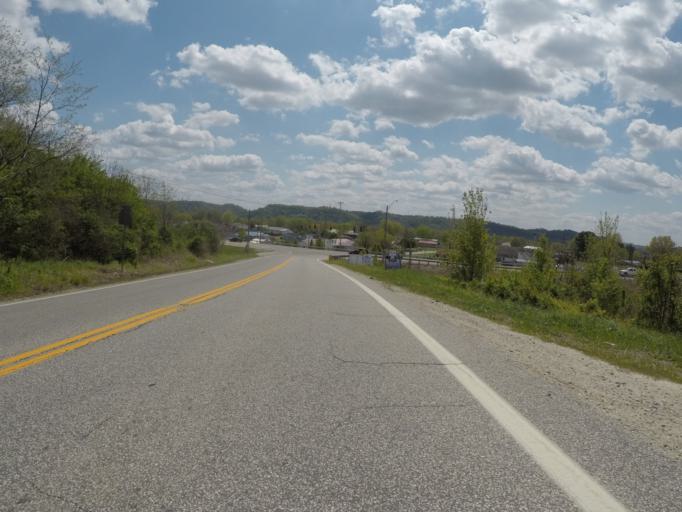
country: US
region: West Virginia
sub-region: Cabell County
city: Pea Ridge
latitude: 38.4493
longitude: -82.3767
